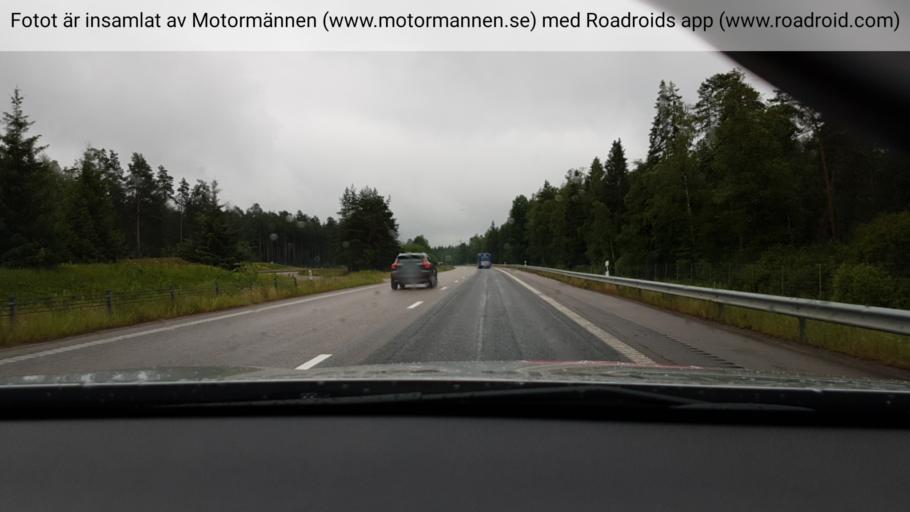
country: SE
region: Uppsala
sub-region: Uppsala Kommun
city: Alsike
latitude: 59.7941
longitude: 17.7728
